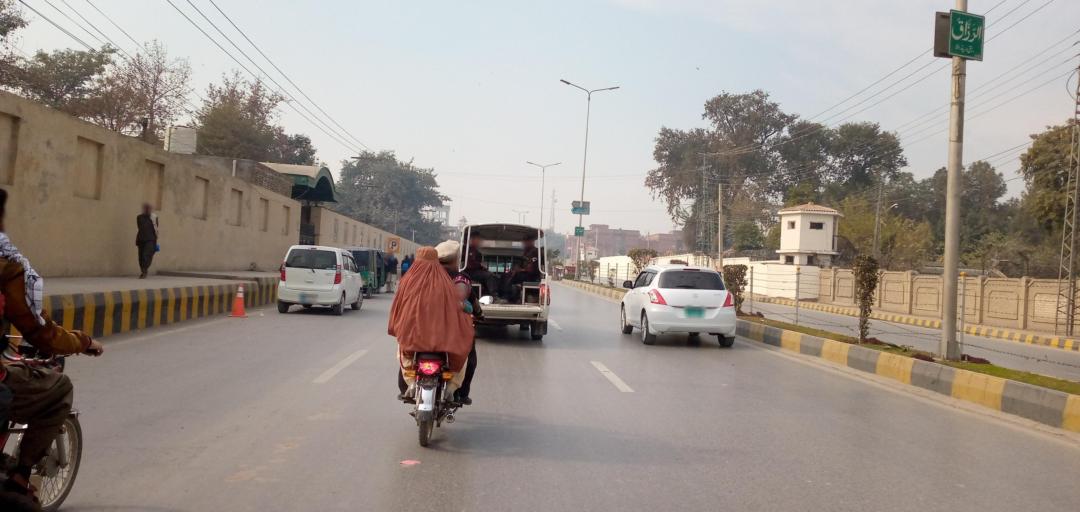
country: PK
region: Khyber Pakhtunkhwa
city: Peshawar
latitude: 34.0145
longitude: 71.5616
